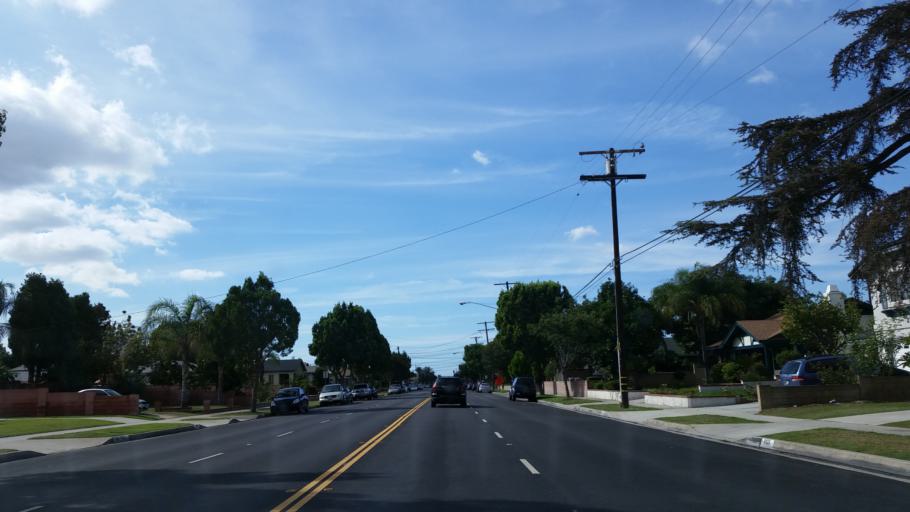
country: US
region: California
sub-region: Los Angeles County
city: Paramount
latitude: 33.8821
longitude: -118.1393
